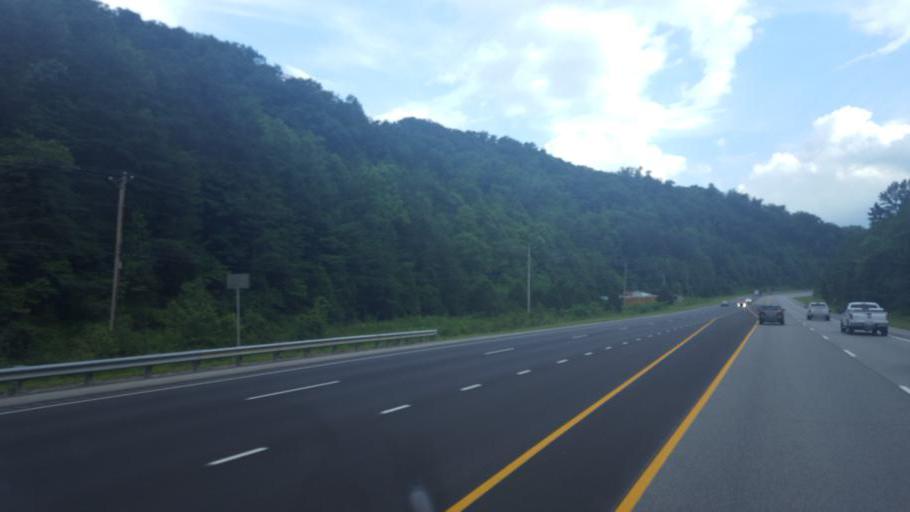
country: US
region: Kentucky
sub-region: Pike County
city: Pikeville
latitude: 37.4243
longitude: -82.5170
